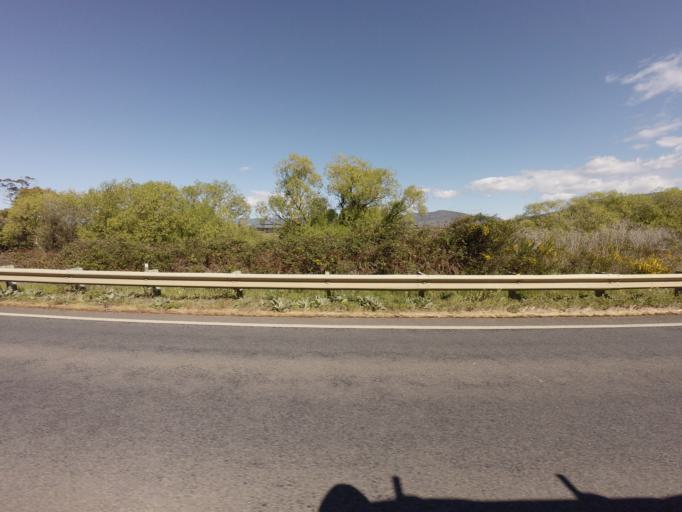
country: AU
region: Tasmania
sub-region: Derwent Valley
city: New Norfolk
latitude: -42.7330
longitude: 146.9685
